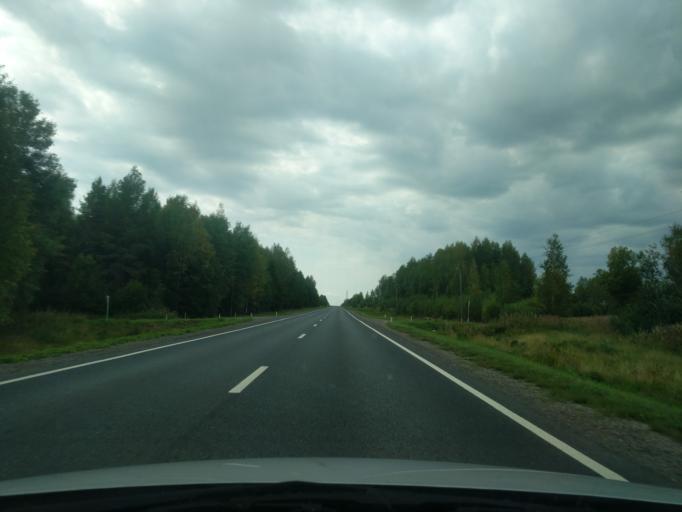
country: RU
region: Kostroma
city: Manturovo
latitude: 58.1511
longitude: 44.3742
